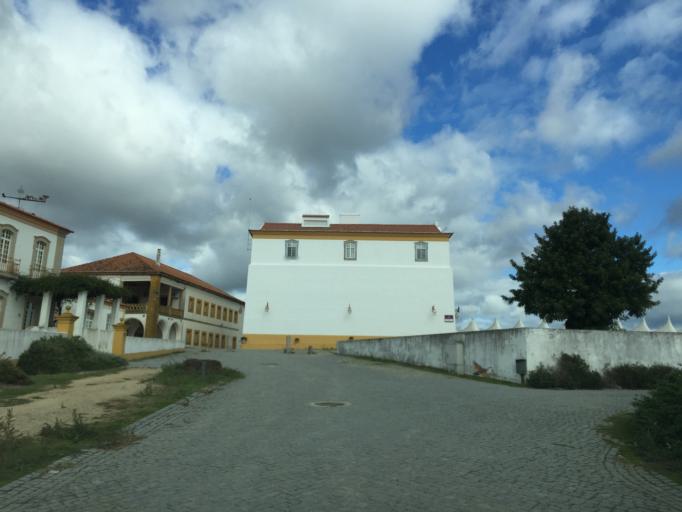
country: PT
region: Portalegre
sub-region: Alter do Chao
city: Alter do Chao
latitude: 39.2220
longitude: -7.6873
